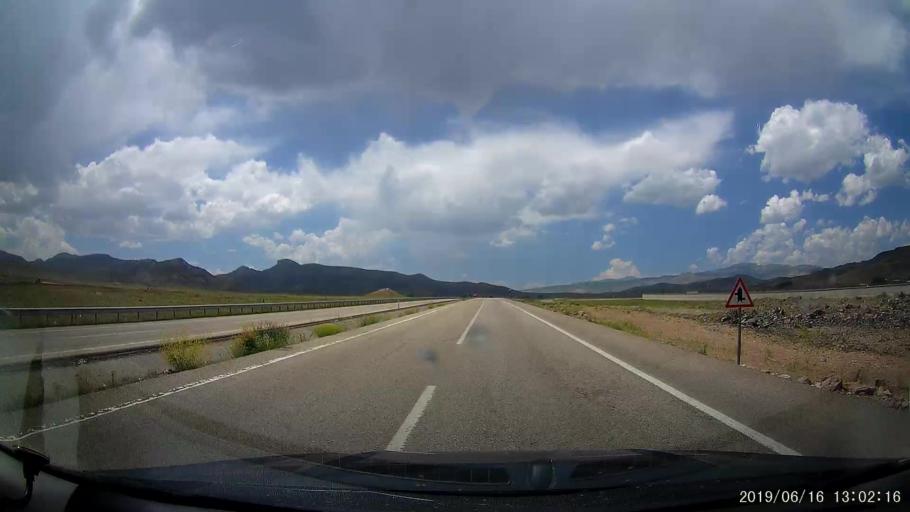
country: TR
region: Agri
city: Sulucem
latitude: 39.5736
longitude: 43.8206
